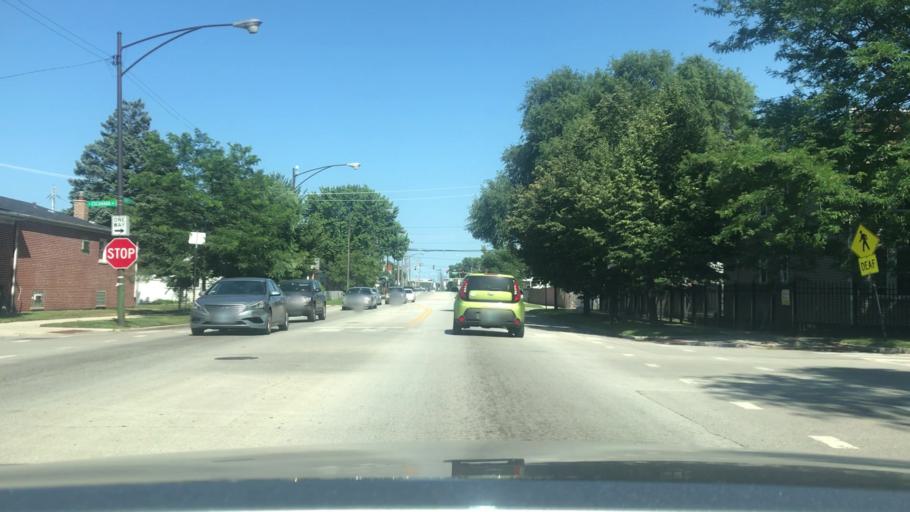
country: US
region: Indiana
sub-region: Lake County
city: Whiting
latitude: 41.7134
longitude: -87.5539
